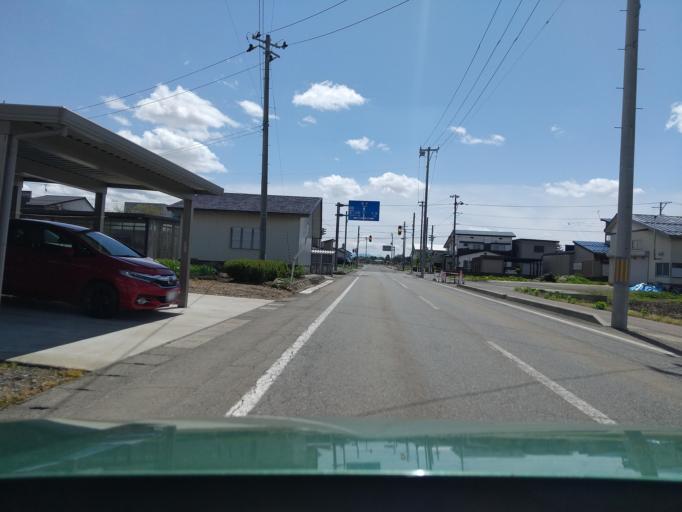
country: JP
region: Akita
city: Yokotemachi
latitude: 39.3654
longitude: 140.5365
